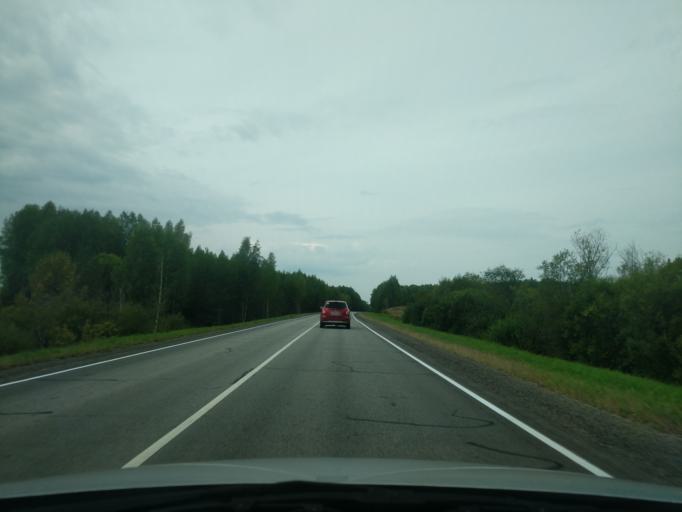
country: RU
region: Kirov
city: Kotel'nich
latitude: 58.2709
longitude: 48.0990
